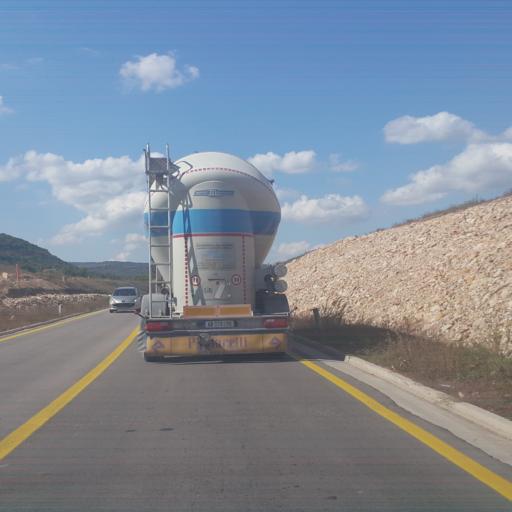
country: RS
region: Central Serbia
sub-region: Pirotski Okrug
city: Bela Palanka
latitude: 43.2603
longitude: 22.2563
